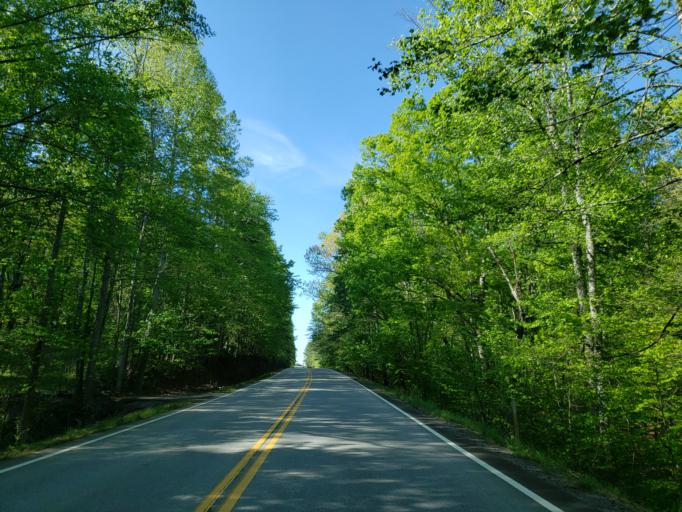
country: US
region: Georgia
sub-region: Haralson County
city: Tallapoosa
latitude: 33.8955
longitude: -85.3117
